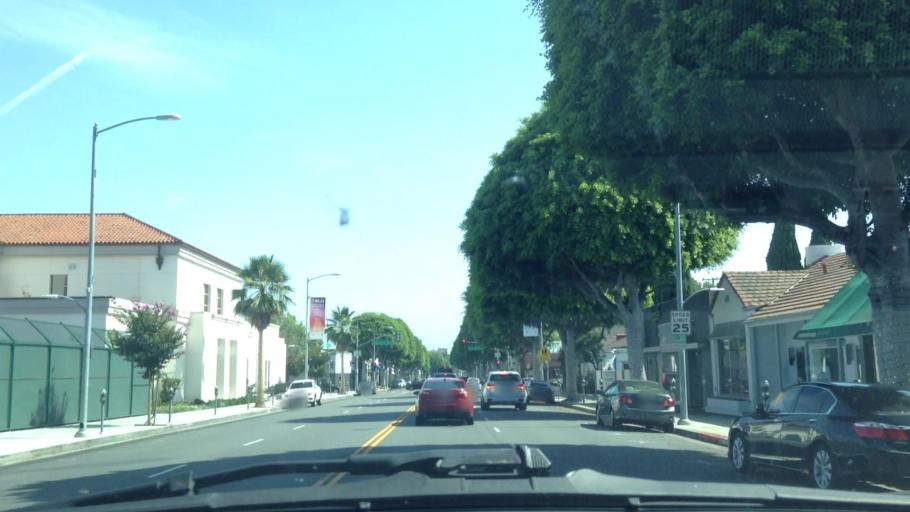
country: US
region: California
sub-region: Los Angeles County
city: Beverly Hills
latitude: 34.0661
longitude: -118.3837
